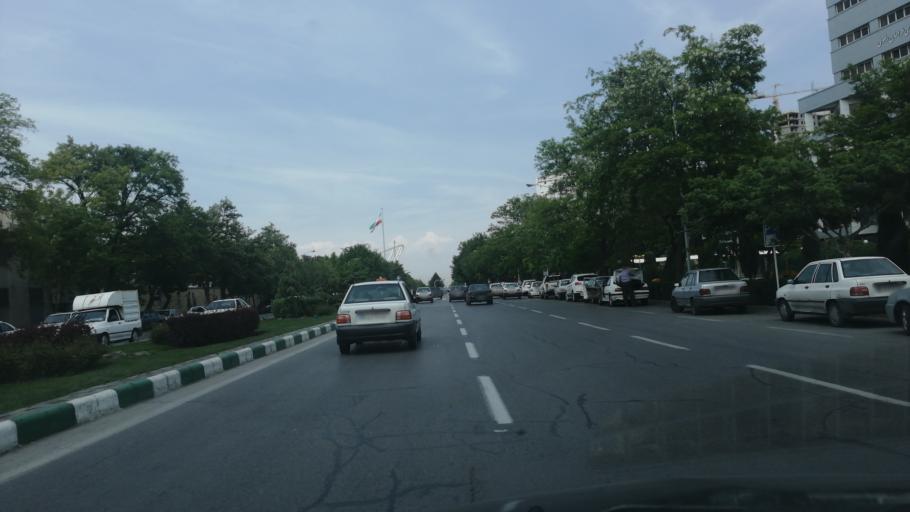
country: IR
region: Razavi Khorasan
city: Mashhad
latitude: 36.3215
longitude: 59.5673
